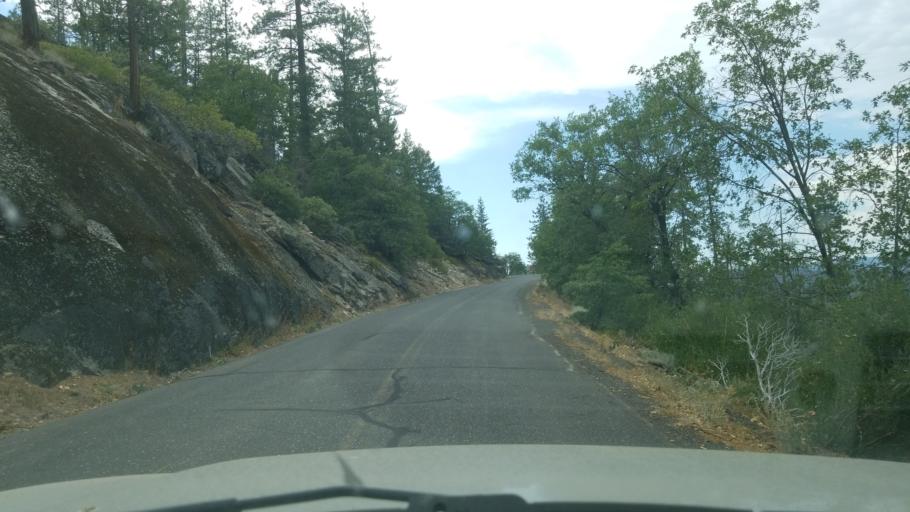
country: US
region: California
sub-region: Mariposa County
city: Yosemite Valley
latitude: 37.9034
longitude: -119.8263
